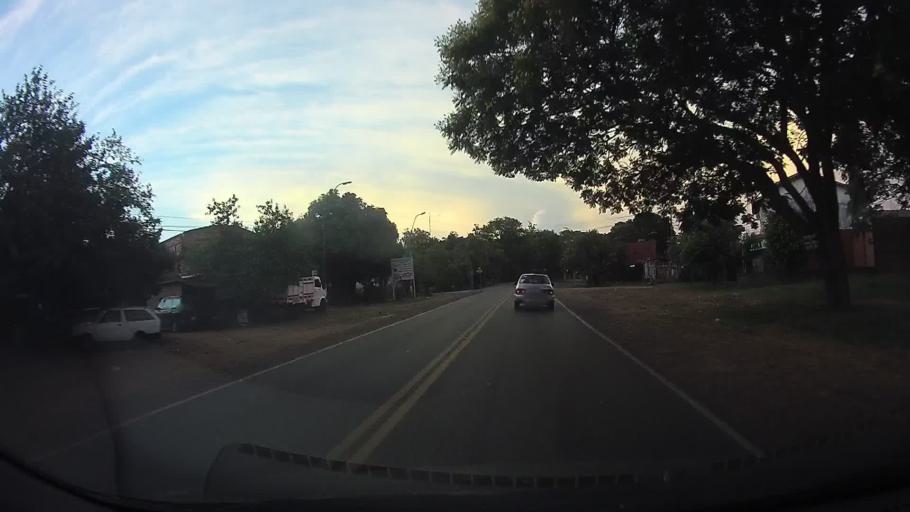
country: PY
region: Central
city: Ita
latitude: -25.5115
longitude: -57.3564
